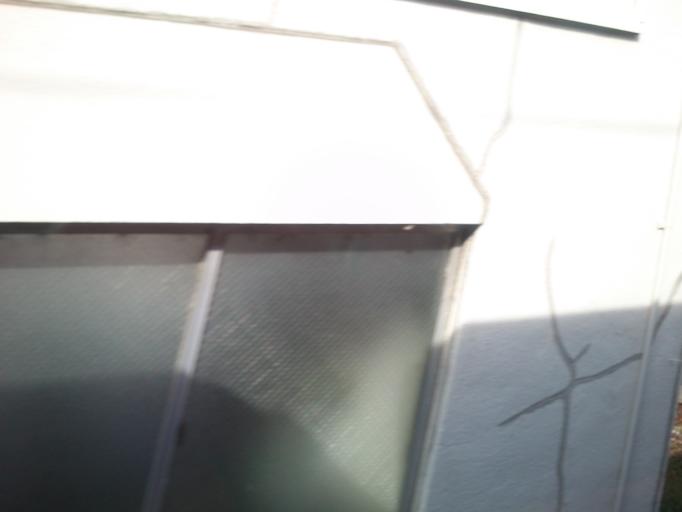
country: JP
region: Hyogo
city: Itami
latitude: 34.7726
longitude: 135.4155
